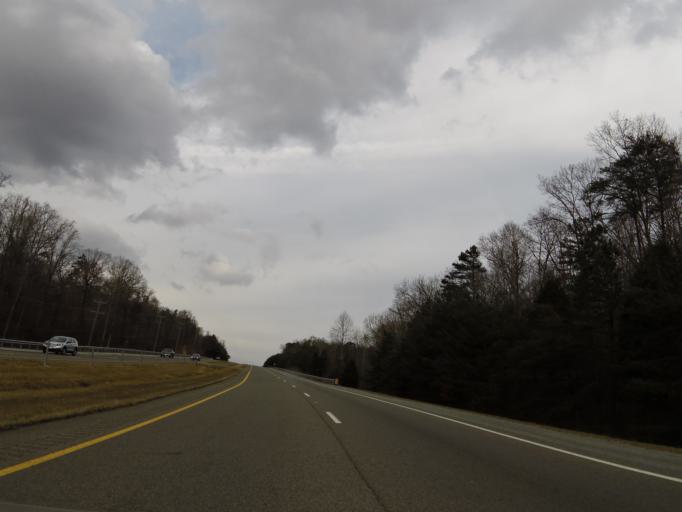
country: US
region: Tennessee
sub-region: Hamilton County
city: Sale Creek
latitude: 35.3097
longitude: -85.1420
